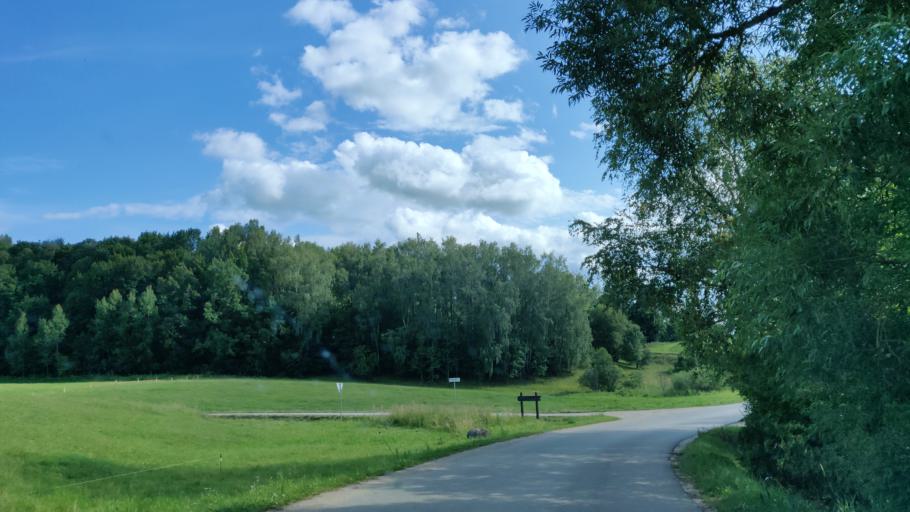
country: LT
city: Varniai
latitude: 55.5995
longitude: 22.3144
